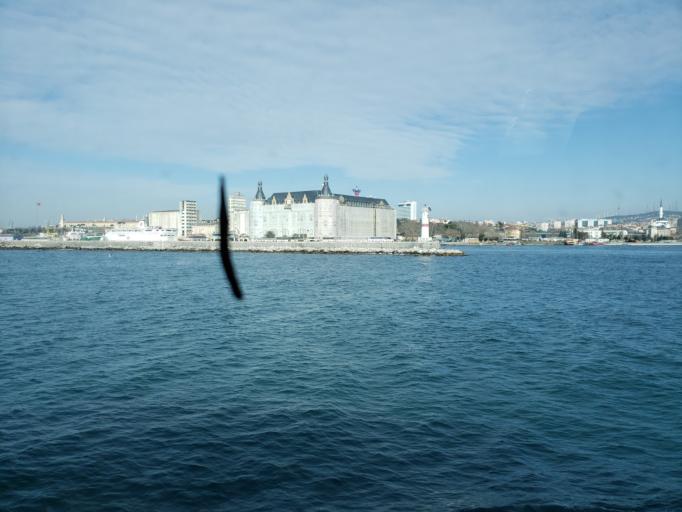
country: TR
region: Istanbul
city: UEskuedar
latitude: 40.9929
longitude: 29.0176
